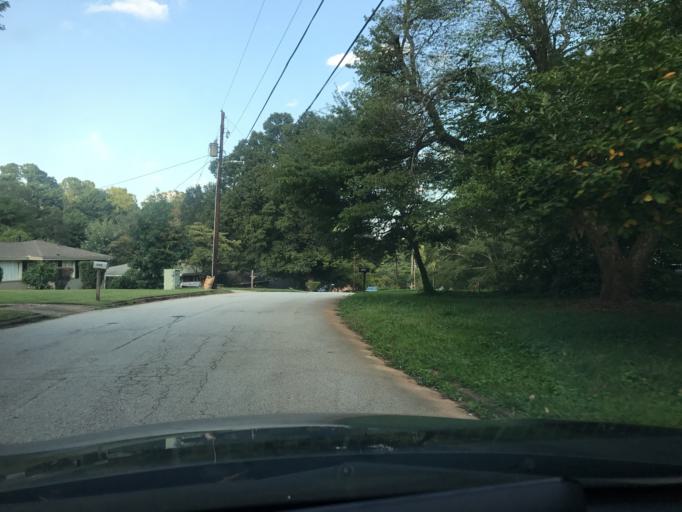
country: US
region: Georgia
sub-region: DeKalb County
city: Belvedere Park
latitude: 33.7502
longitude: -84.2627
